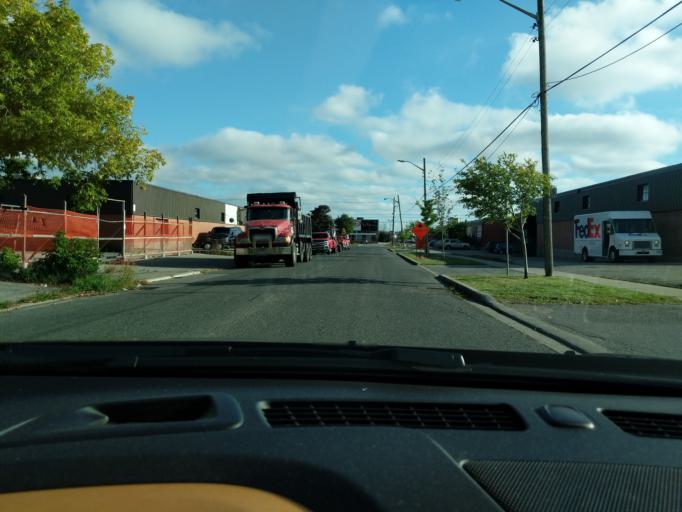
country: CA
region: Ontario
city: Toronto
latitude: 43.7202
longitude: -79.4622
